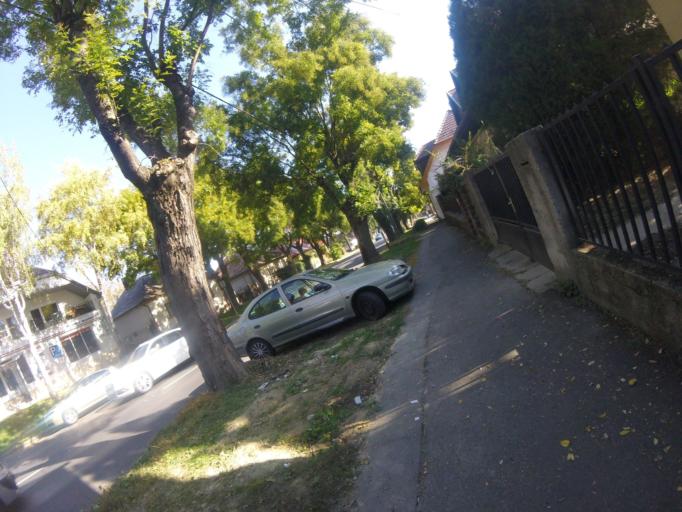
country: HU
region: Zala
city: Keszthely
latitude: 46.7702
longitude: 17.2553
